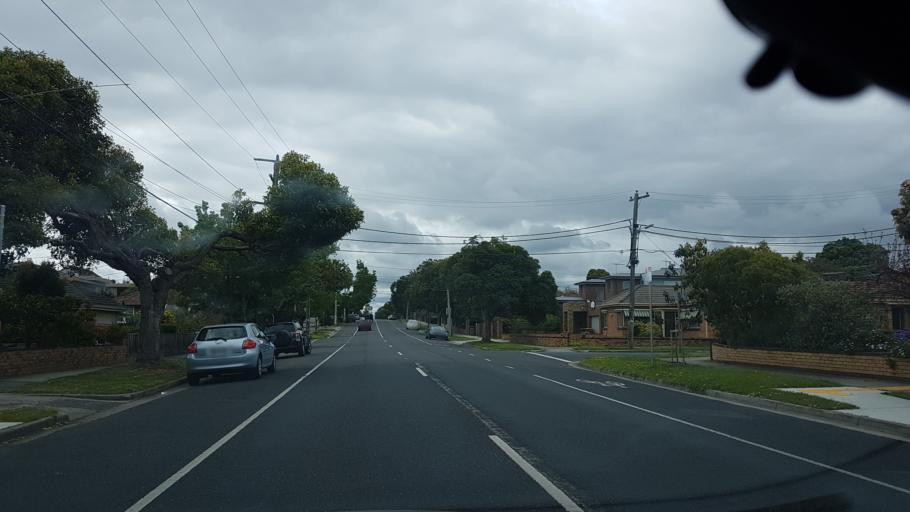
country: AU
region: Victoria
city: McKinnon
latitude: -37.9258
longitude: 145.0500
